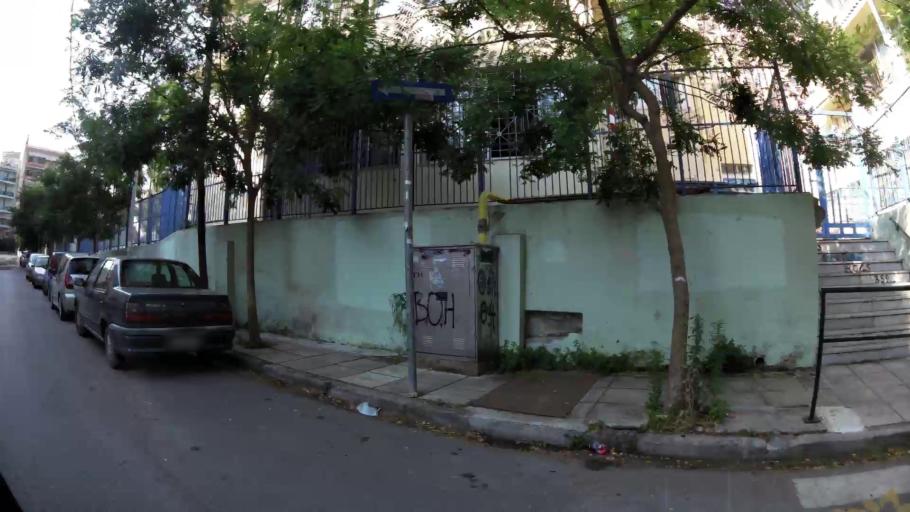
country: GR
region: Central Macedonia
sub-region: Nomos Thessalonikis
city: Sykies
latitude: 40.6530
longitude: 22.9573
